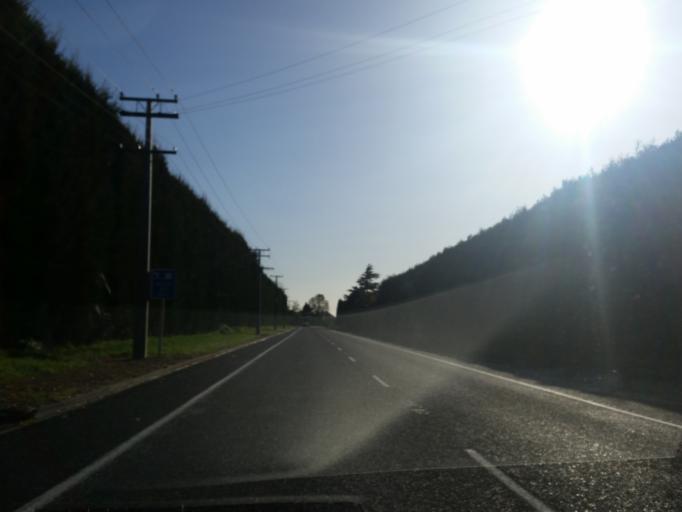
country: NZ
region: Bay of Plenty
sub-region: Western Bay of Plenty District
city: Katikati
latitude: -37.5095
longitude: 175.9210
